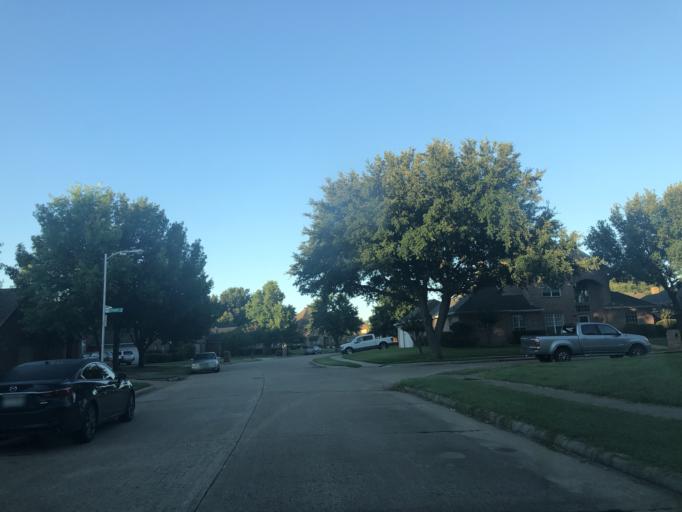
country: US
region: Texas
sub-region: Dallas County
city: Grand Prairie
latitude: 32.6677
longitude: -96.9983
